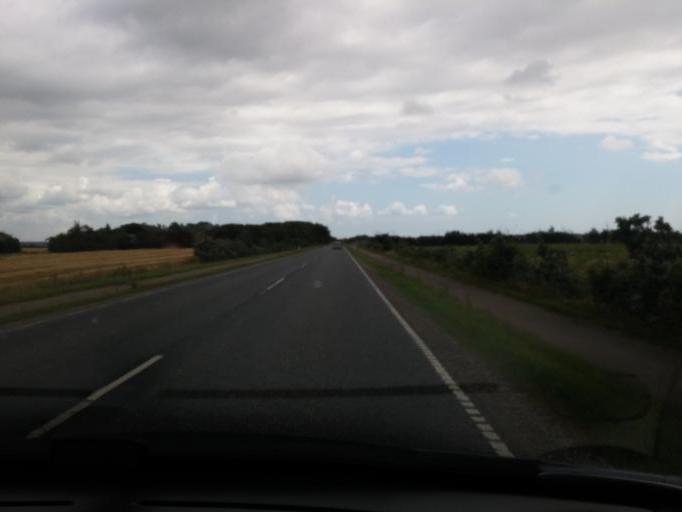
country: DK
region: South Denmark
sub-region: Langeland Kommune
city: Rudkobing
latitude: 54.9558
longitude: 10.6830
